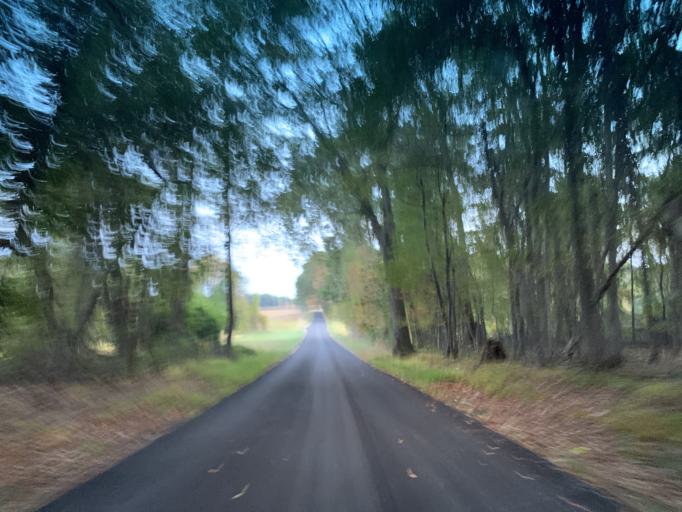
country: US
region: Pennsylvania
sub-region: York County
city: Stewartstown
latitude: 39.6698
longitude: -76.6291
